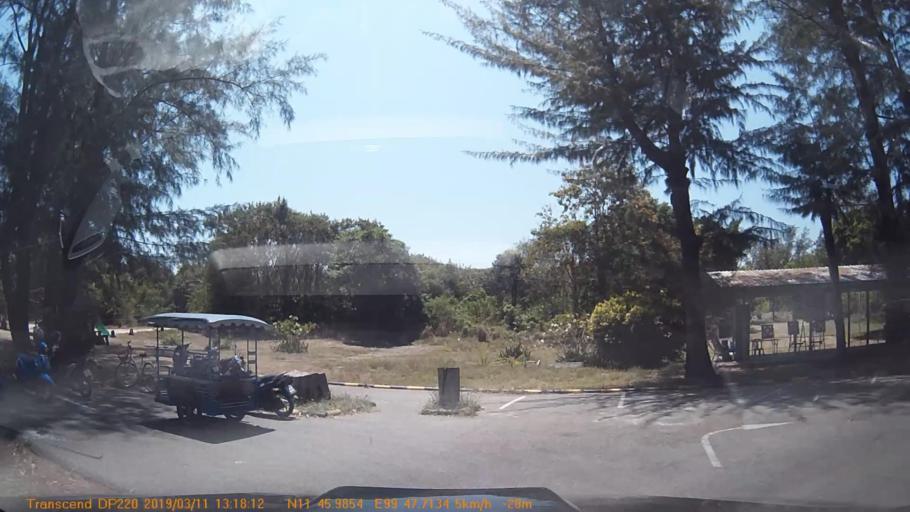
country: TH
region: Prachuap Khiri Khan
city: Prachuap Khiri Khan
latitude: 11.7664
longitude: 99.7952
